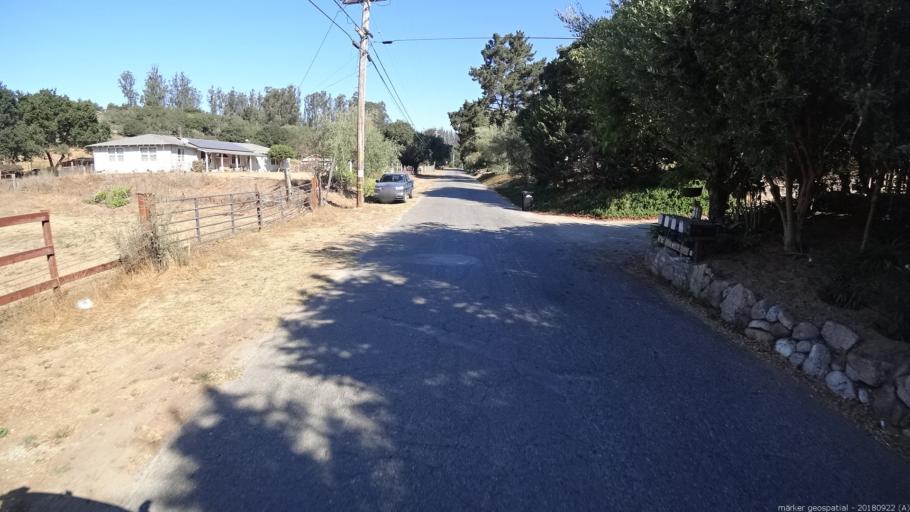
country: US
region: California
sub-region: Monterey County
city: Prunedale
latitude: 36.8167
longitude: -121.6547
